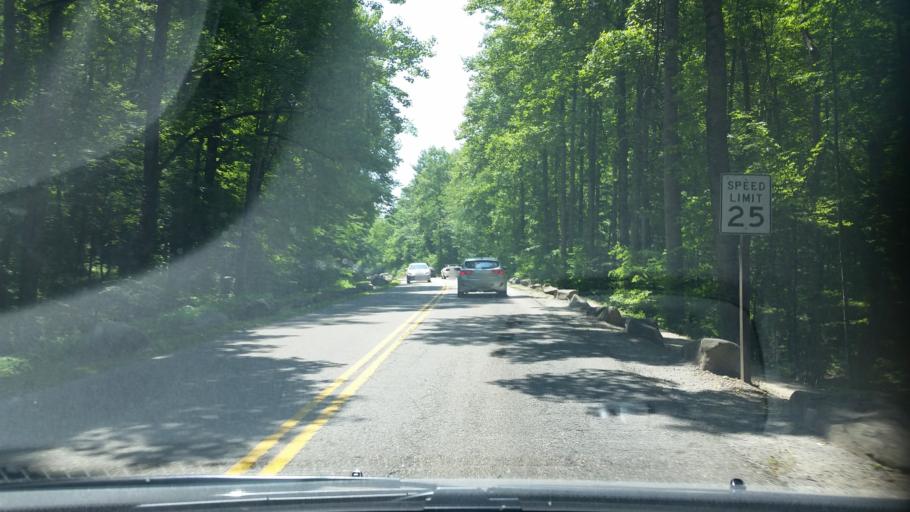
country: US
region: Tennessee
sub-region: Sevier County
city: Gatlinburg
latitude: 35.6725
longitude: -83.5782
